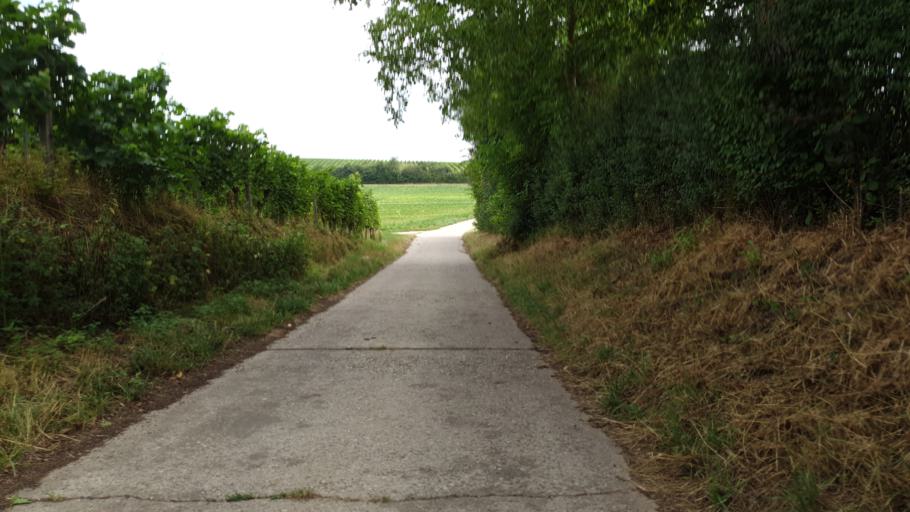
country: DE
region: Rheinland-Pfalz
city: Billigheim-Ingenheim
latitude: 49.1236
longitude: 8.0847
